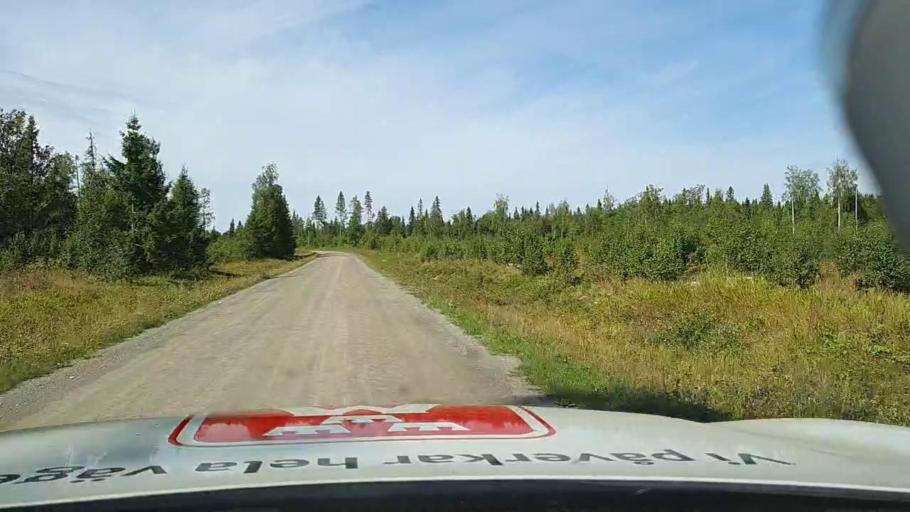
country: SE
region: Jaemtland
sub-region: Stroemsunds Kommun
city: Stroemsund
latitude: 63.7177
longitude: 15.2949
